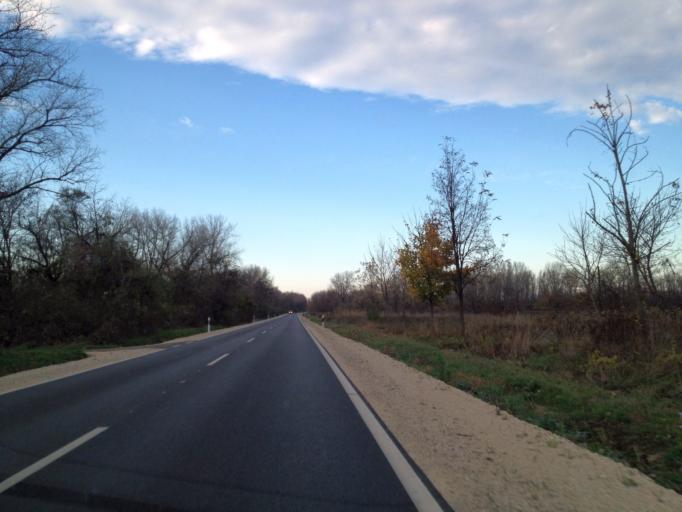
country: HU
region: Gyor-Moson-Sopron
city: Nyul
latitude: 47.6070
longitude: 17.6859
